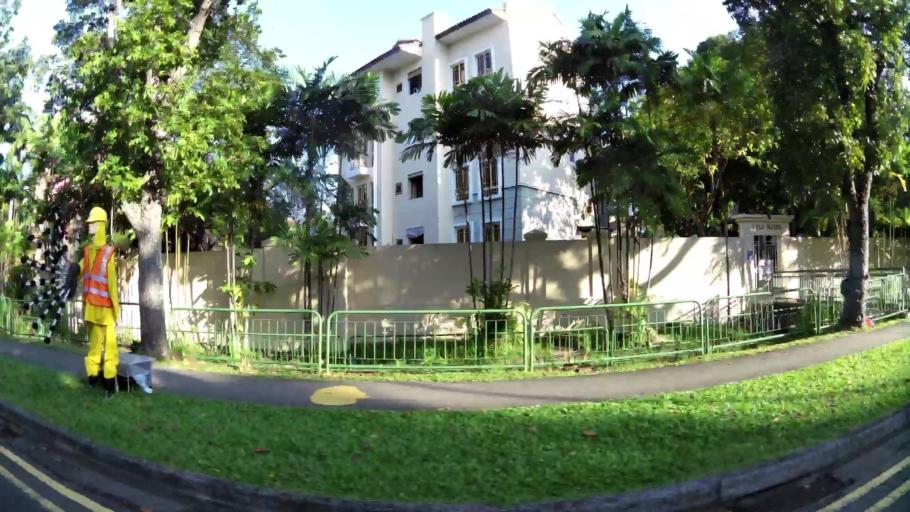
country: SG
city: Singapore
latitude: 1.3093
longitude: 103.9272
